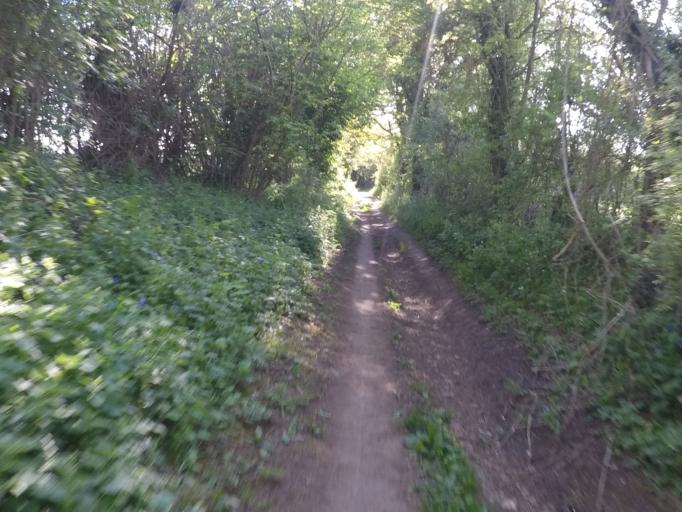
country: GB
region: England
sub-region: Oxfordshire
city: Charlbury
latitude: 51.8750
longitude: -1.4622
